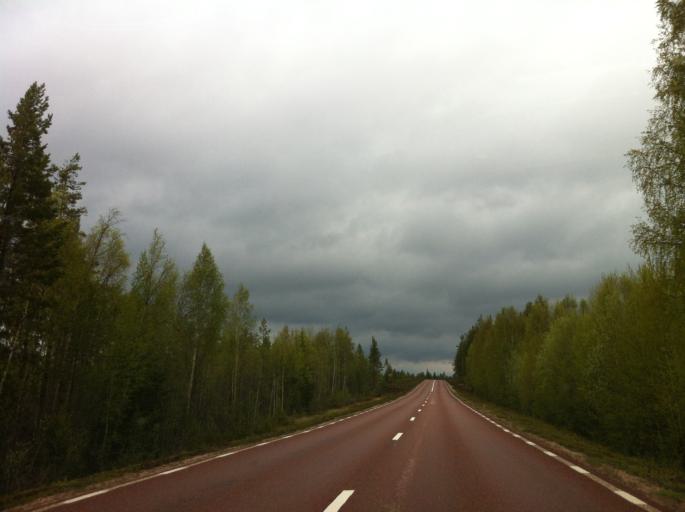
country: SE
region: Jaemtland
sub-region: Harjedalens Kommun
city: Sveg
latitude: 61.9011
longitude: 14.6223
